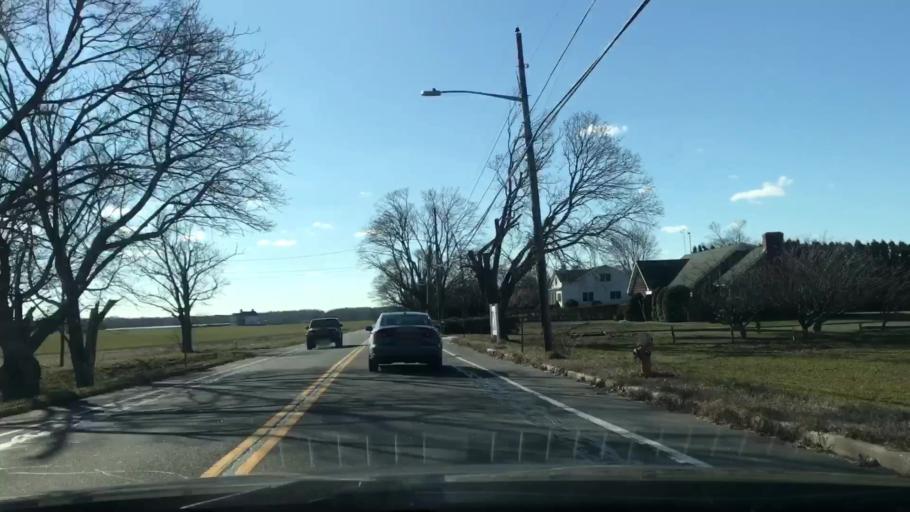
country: US
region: New York
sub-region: Suffolk County
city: Aquebogue
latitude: 40.9531
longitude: -72.6537
